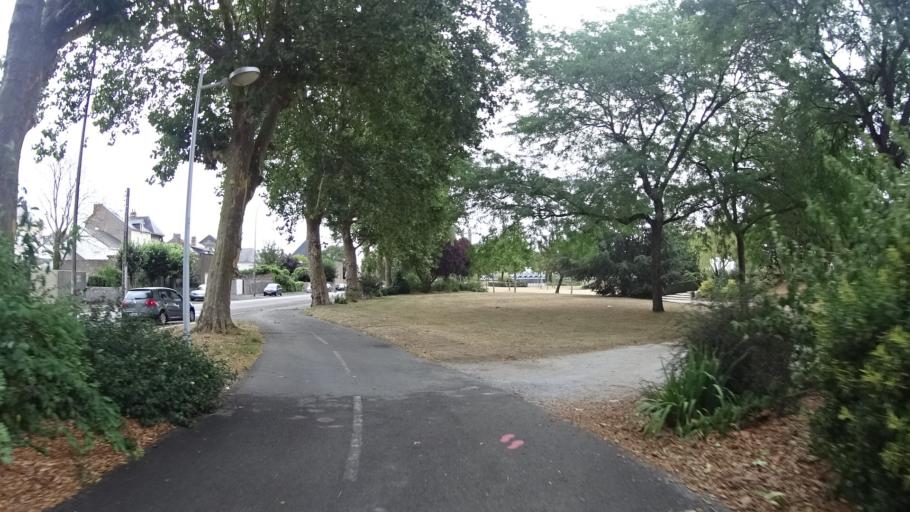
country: FR
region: Pays de la Loire
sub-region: Departement de la Loire-Atlantique
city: Ancenis
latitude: 47.3633
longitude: -1.1816
